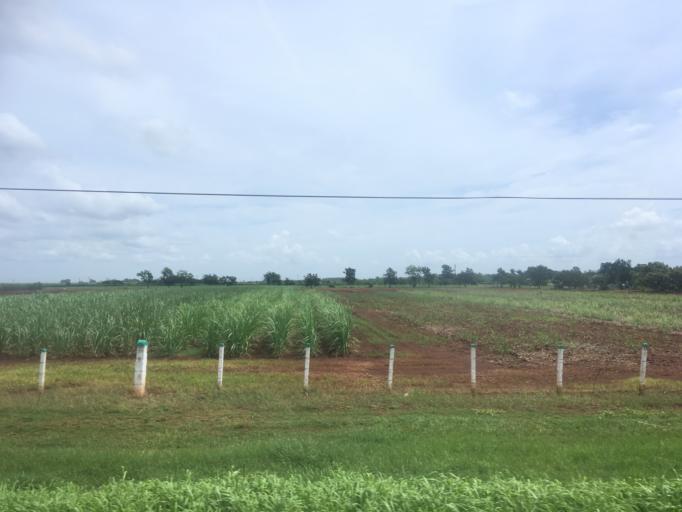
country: CU
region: Matanzas
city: Jovellanos
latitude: 22.7966
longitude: -81.1456
